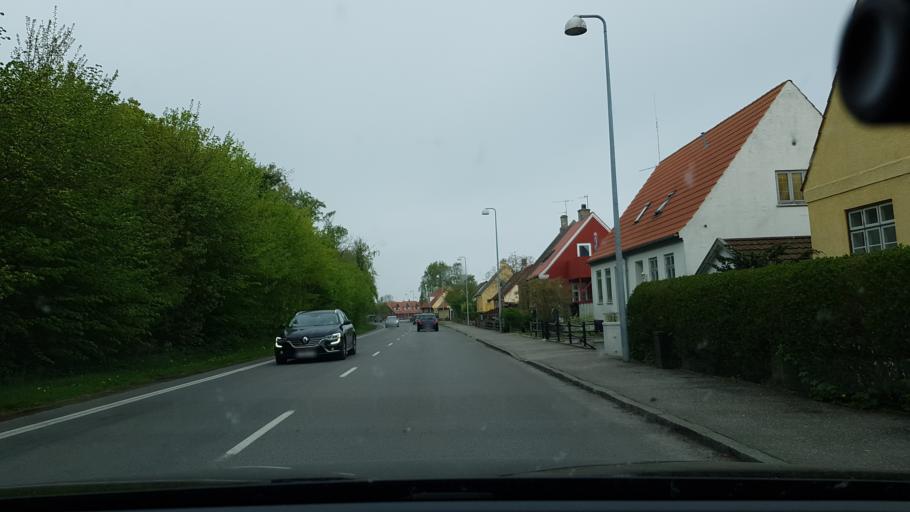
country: DK
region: Capital Region
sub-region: Bornholm Kommune
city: Nexo
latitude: 55.0553
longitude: 15.1255
